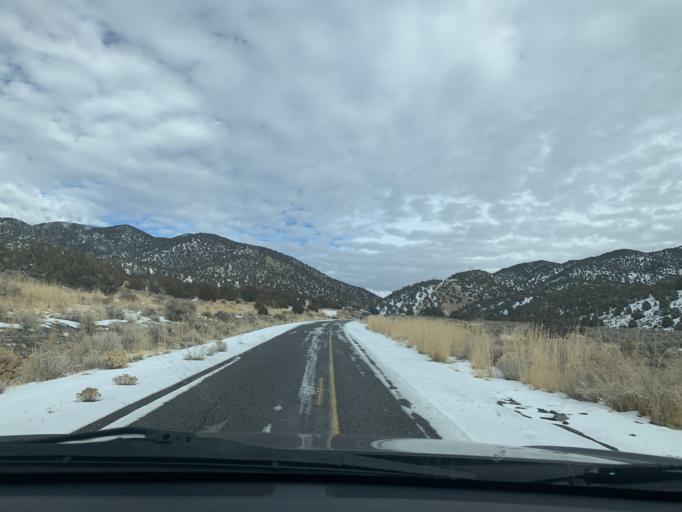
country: US
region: Utah
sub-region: Tooele County
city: Tooele
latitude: 40.3057
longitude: -112.2604
